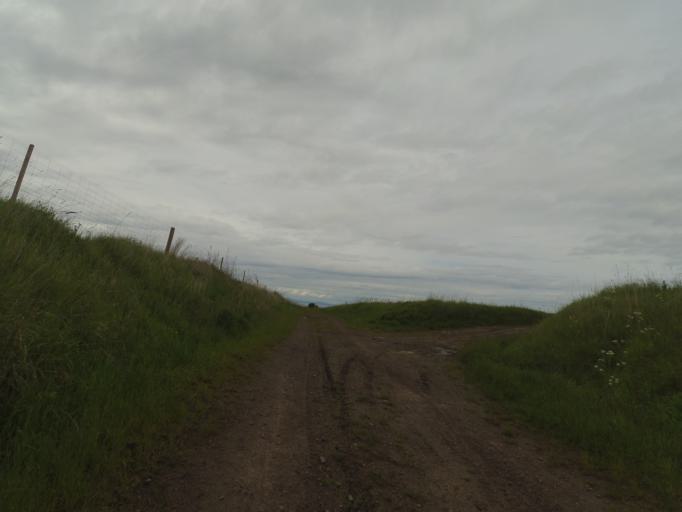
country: GB
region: Scotland
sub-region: East Lothian
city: Macmerry
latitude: 55.9520
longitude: -2.9247
